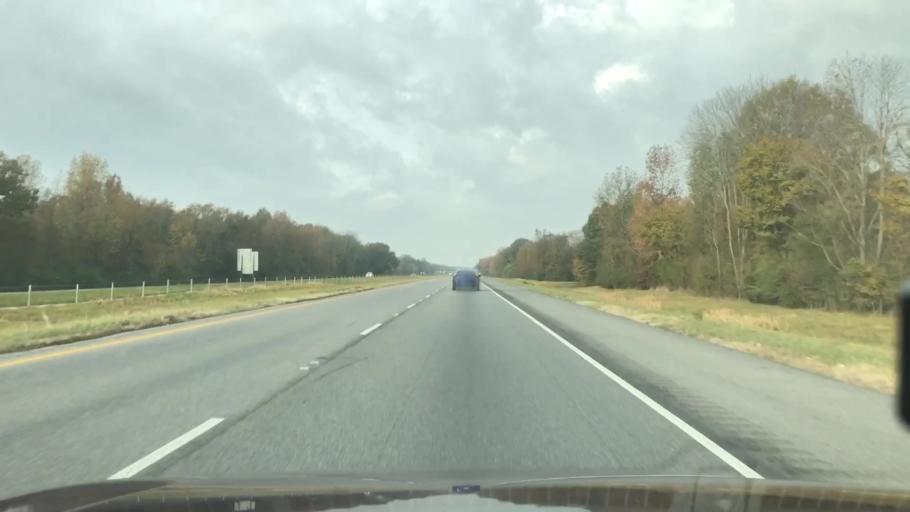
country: US
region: Louisiana
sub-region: Richland Parish
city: Delhi
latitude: 32.4451
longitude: -91.5125
